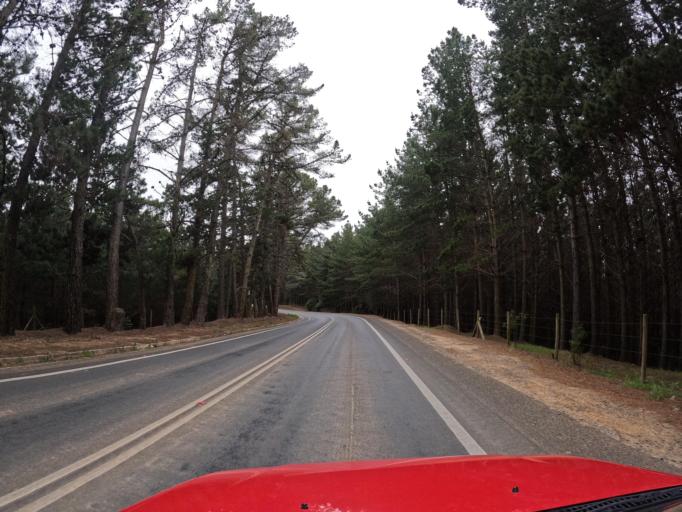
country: CL
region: O'Higgins
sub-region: Provincia de Colchagua
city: Santa Cruz
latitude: -34.5758
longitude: -72.0155
